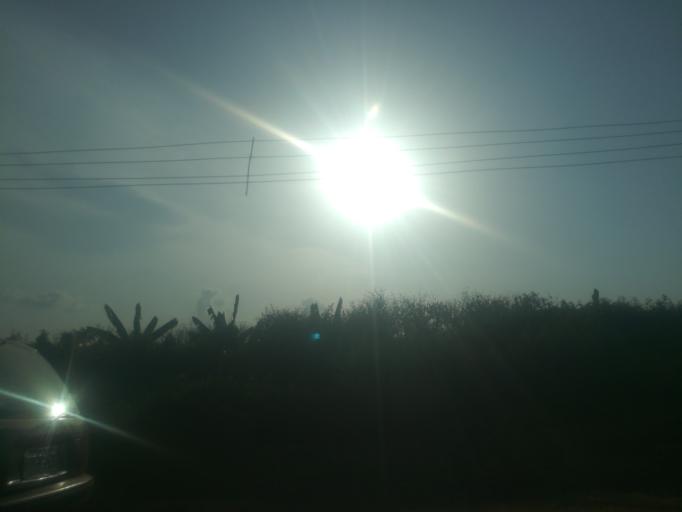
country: NG
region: Oyo
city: Moniya
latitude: 7.5571
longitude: 3.8883
